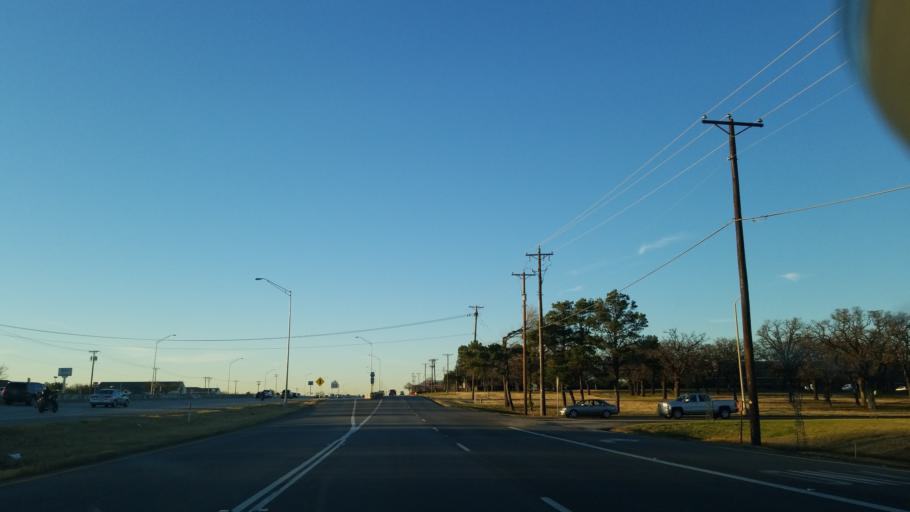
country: US
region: Texas
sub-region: Denton County
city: Hickory Creek
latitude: 33.1364
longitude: -97.0454
